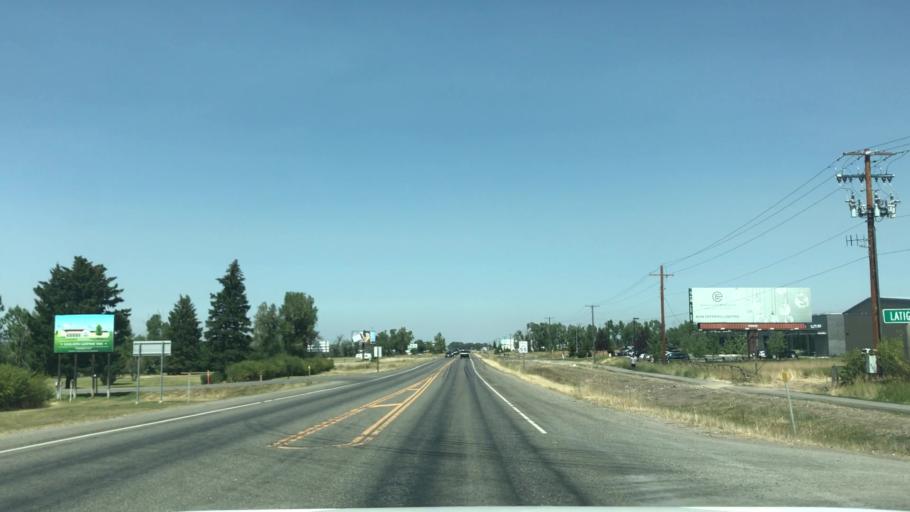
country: US
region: Montana
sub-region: Gallatin County
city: Four Corners
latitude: 45.5929
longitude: -111.1970
